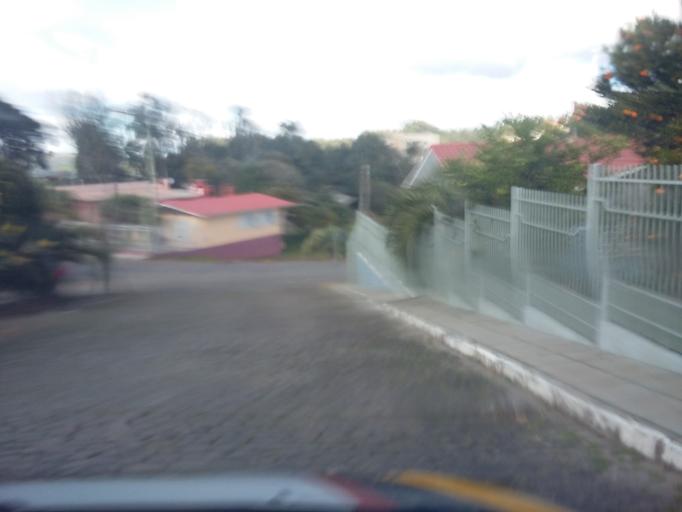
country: BR
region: Rio Grande do Sul
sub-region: Sao Marcos
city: Sao Marcos
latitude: -28.7977
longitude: -51.0925
